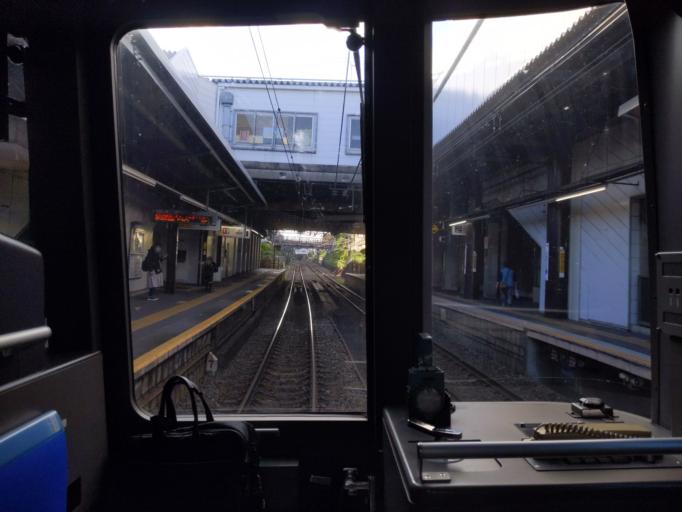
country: JP
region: Tokyo
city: Tokyo
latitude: 35.6626
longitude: 139.6610
